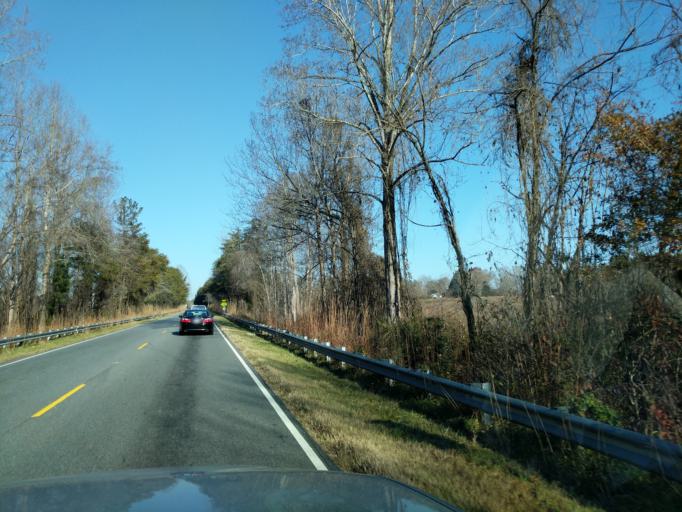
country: US
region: North Carolina
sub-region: Rutherford County
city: Rutherfordton
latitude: 35.3932
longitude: -81.9613
